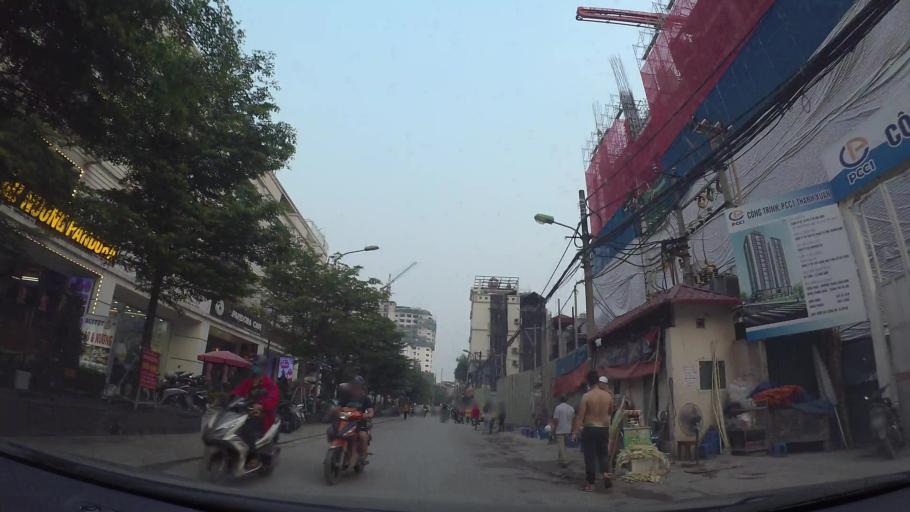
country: VN
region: Ha Noi
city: Thanh Xuan
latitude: 20.9858
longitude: 105.7985
